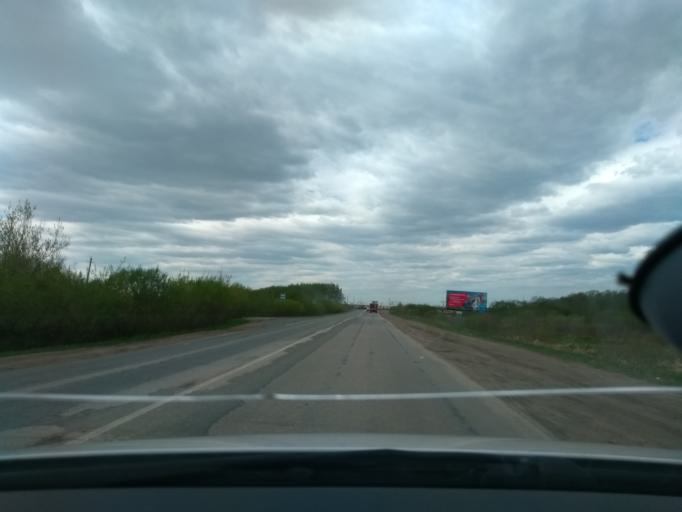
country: RU
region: Perm
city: Lobanovo
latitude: 57.8745
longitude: 56.2773
